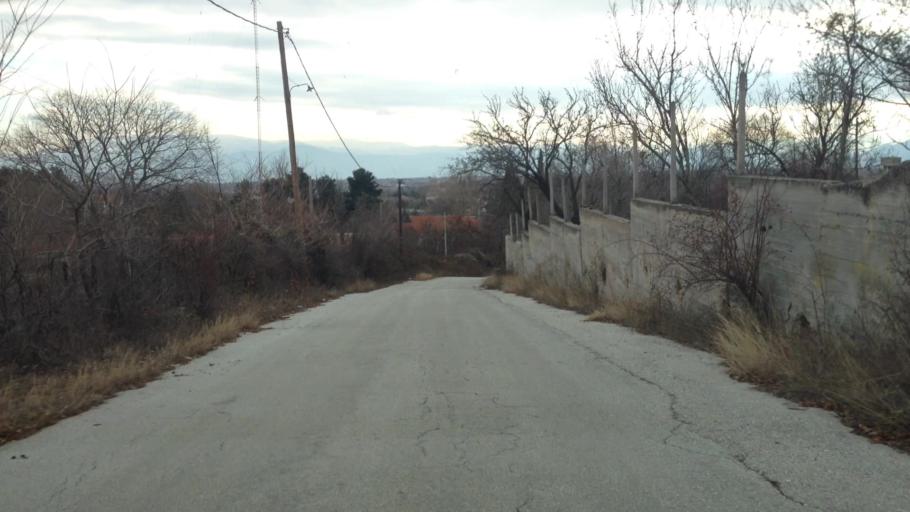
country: GR
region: West Macedonia
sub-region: Nomos Kozanis
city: Kozani
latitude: 40.2914
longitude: 21.7746
